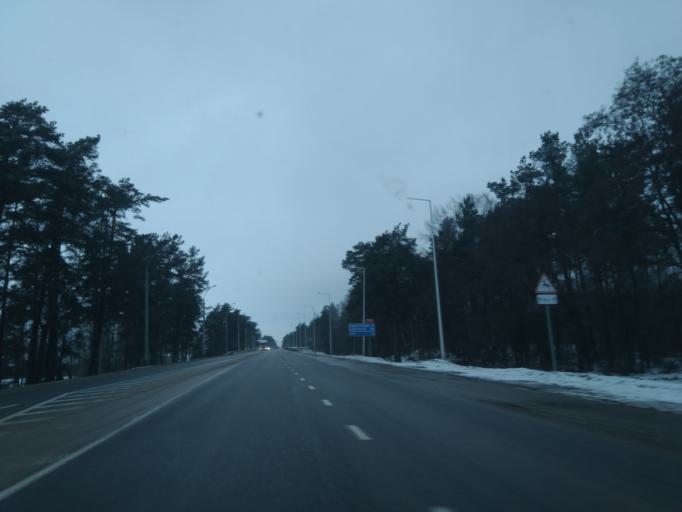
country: BY
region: Minsk
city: Nyasvizh
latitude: 53.2421
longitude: 26.6299
